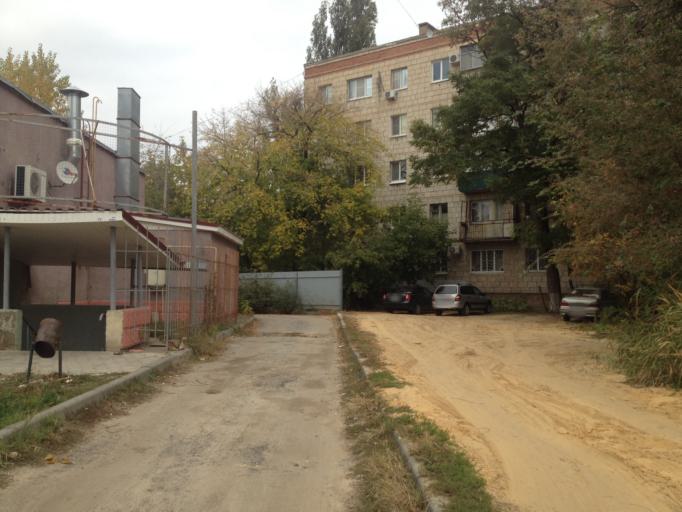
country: RU
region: Volgograd
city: Volgograd
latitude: 48.7367
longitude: 44.4884
